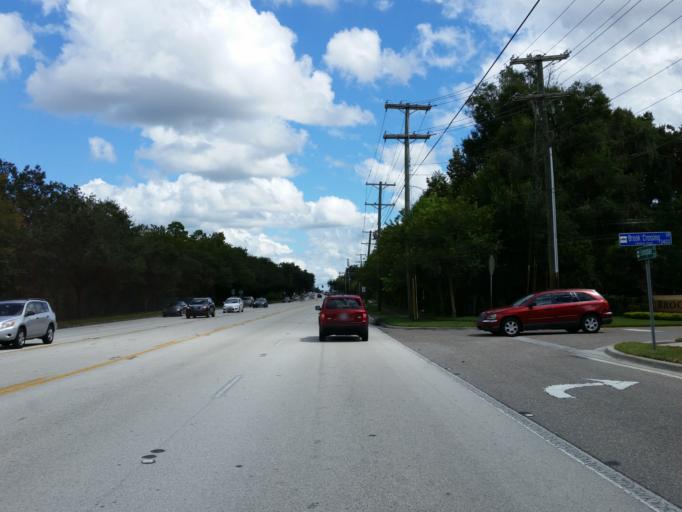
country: US
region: Florida
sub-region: Hillsborough County
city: Bloomingdale
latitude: 27.8936
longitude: -82.2820
